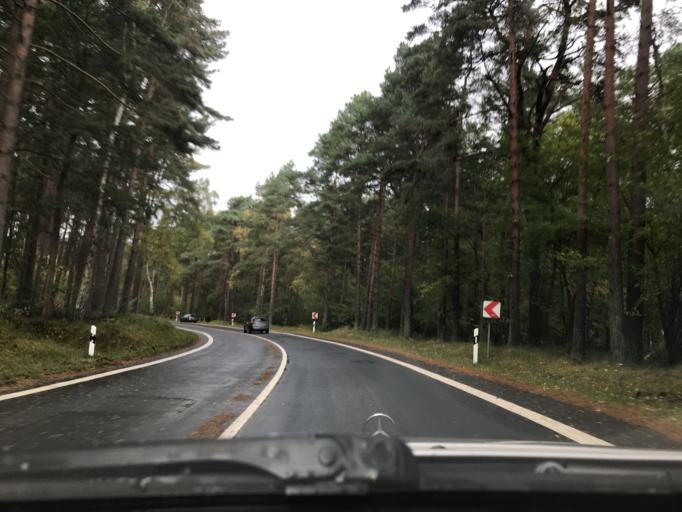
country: DE
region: Mecklenburg-Vorpommern
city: Karlshagen
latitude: 54.1434
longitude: 13.8219
